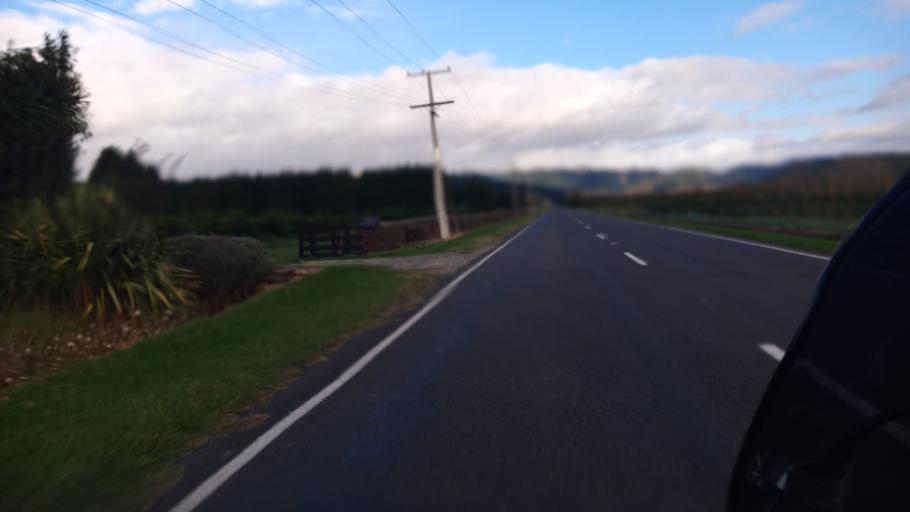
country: NZ
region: Gisborne
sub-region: Gisborne District
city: Gisborne
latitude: -38.6323
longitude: 177.8774
